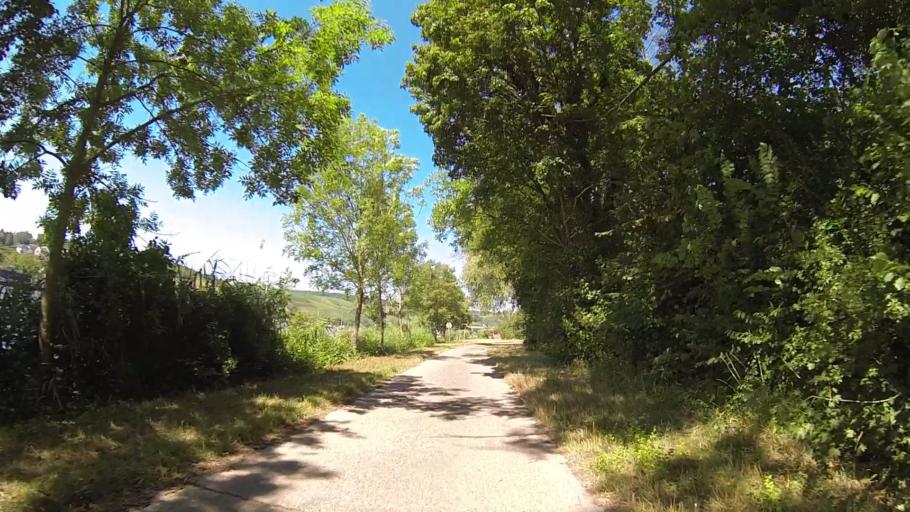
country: DE
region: Rheinland-Pfalz
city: Palzem
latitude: 49.5669
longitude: 6.3679
